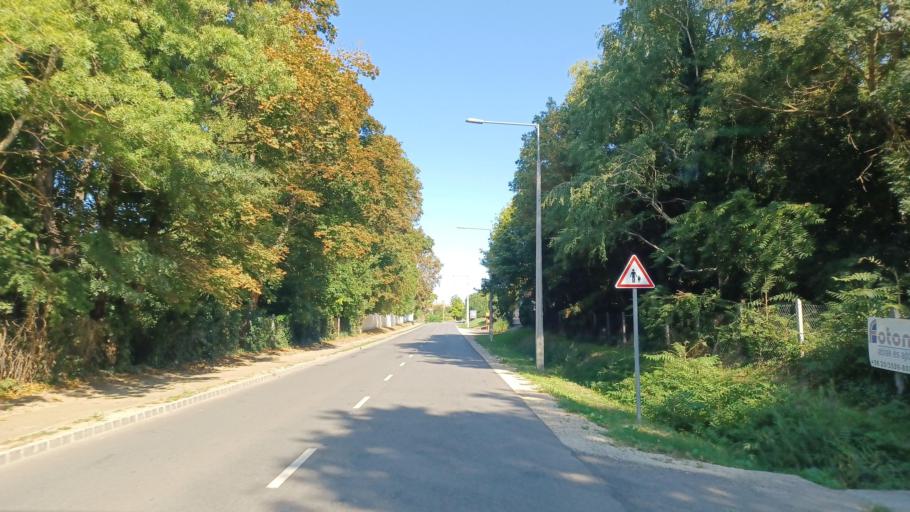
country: HU
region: Tolna
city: Nemetker
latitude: 46.6810
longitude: 18.8064
